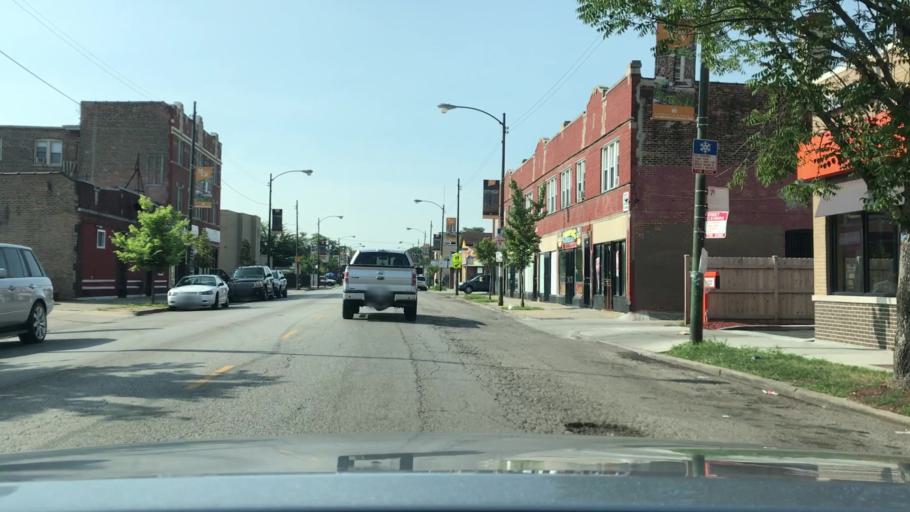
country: US
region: Illinois
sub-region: Cook County
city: Hometown
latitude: 41.7742
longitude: -87.7031
